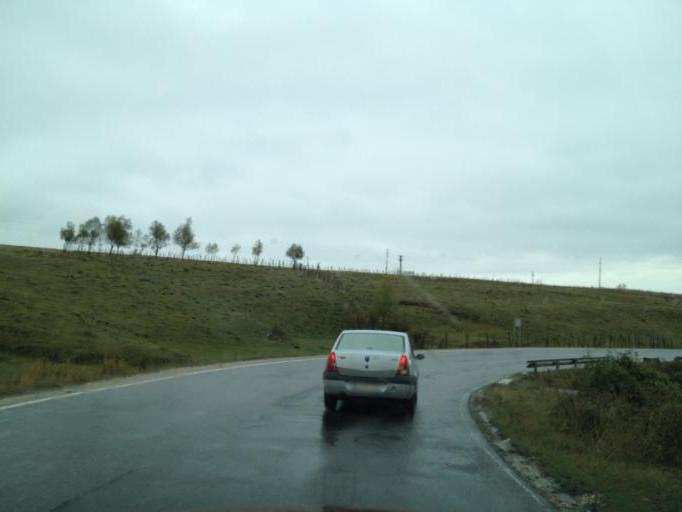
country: RO
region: Arges
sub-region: Comuna Valea Mare-Pravat
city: Valea Mare Pravat
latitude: 45.2959
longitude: 25.1263
